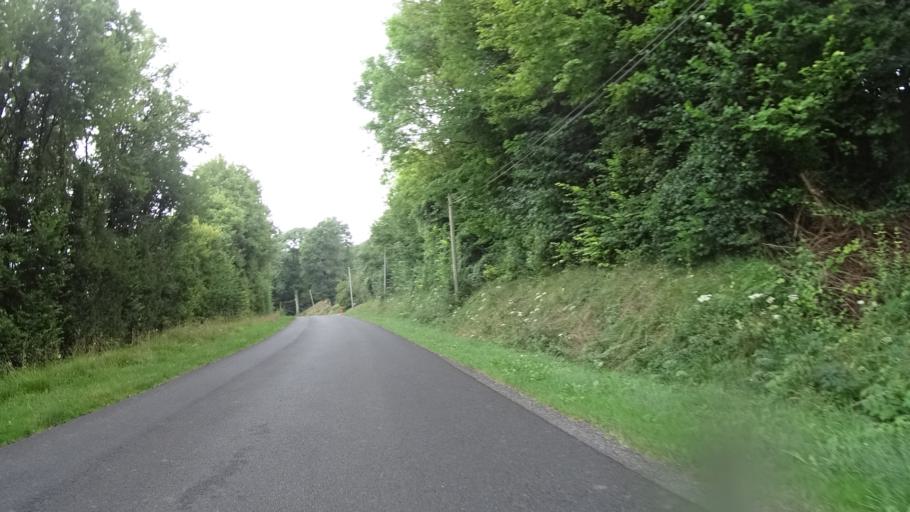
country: FR
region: Centre
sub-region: Departement du Loiret
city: Saint-Germain-des-Pres
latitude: 47.9257
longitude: 2.9019
